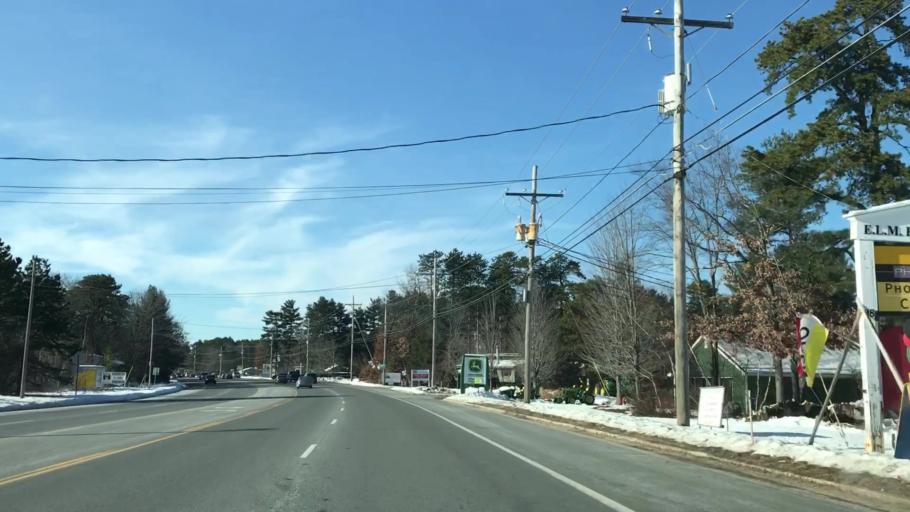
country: US
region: New Hampshire
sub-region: Hillsborough County
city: Hollis
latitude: 42.8104
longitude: -71.5752
